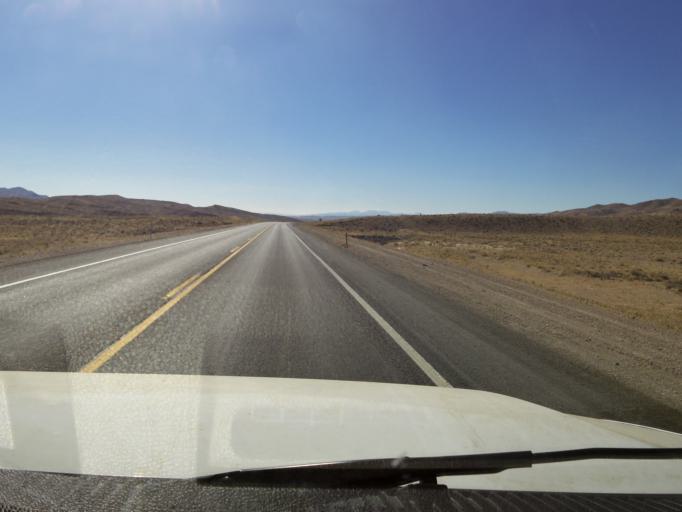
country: US
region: Nevada
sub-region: Esmeralda County
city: Goldfield
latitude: 37.5708
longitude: -117.2014
